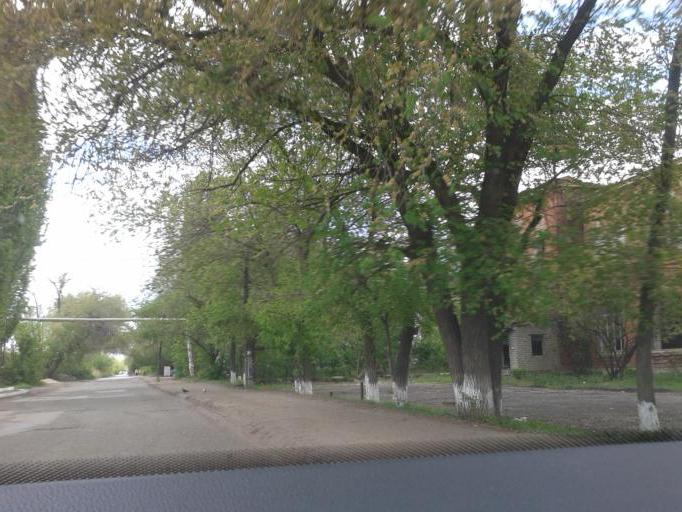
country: RU
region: Volgograd
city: Krasnoslobodsk
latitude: 48.5182
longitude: 44.5166
